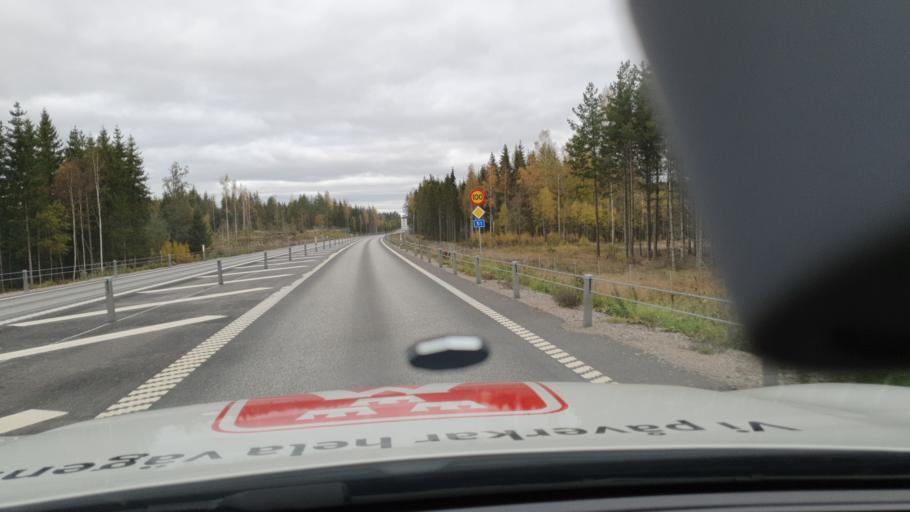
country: SE
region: OErebro
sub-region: Hallsbergs Kommun
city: Palsboda
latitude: 59.0567
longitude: 15.3238
